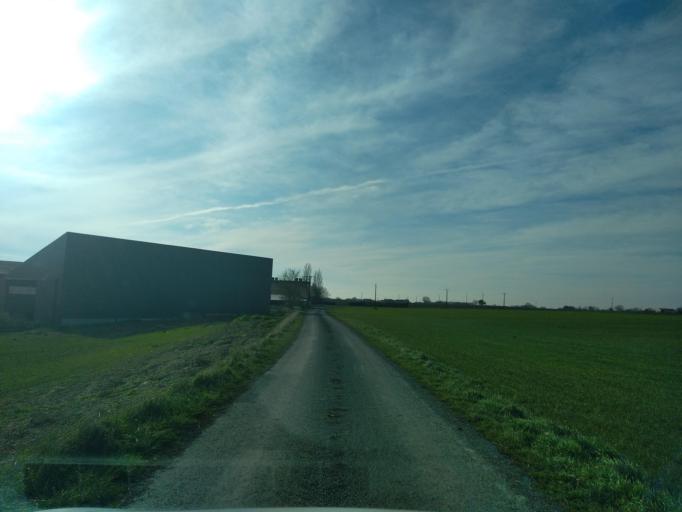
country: FR
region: Pays de la Loire
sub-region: Departement de la Vendee
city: Maillezais
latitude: 46.3518
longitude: -0.7466
